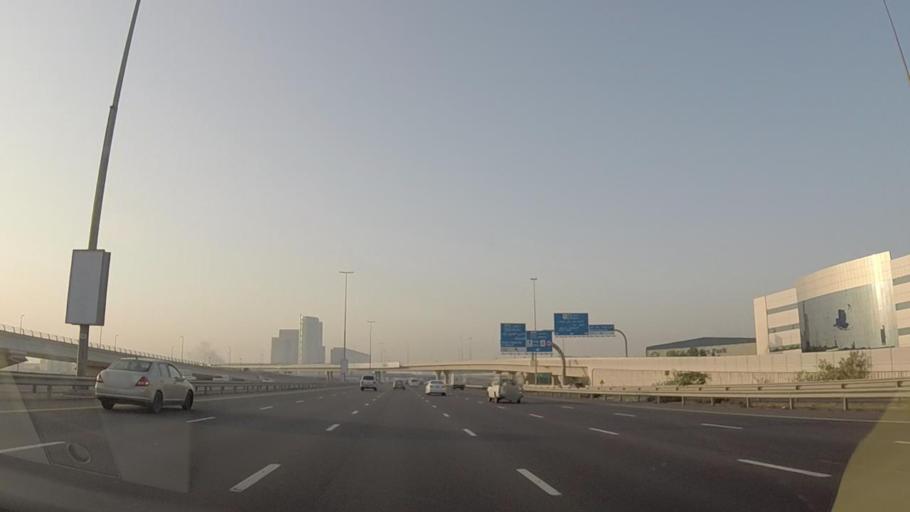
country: AE
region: Dubai
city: Dubai
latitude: 24.9938
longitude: 55.0939
